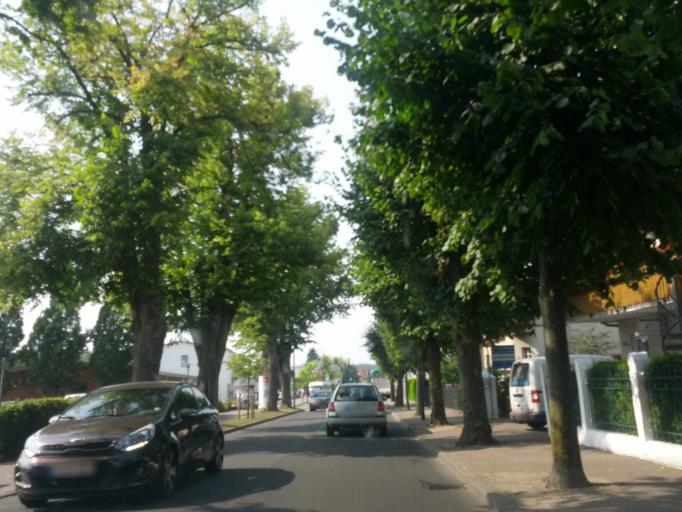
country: DE
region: Mecklenburg-Vorpommern
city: Ostseebad Binz
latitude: 54.3925
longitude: 13.6113
